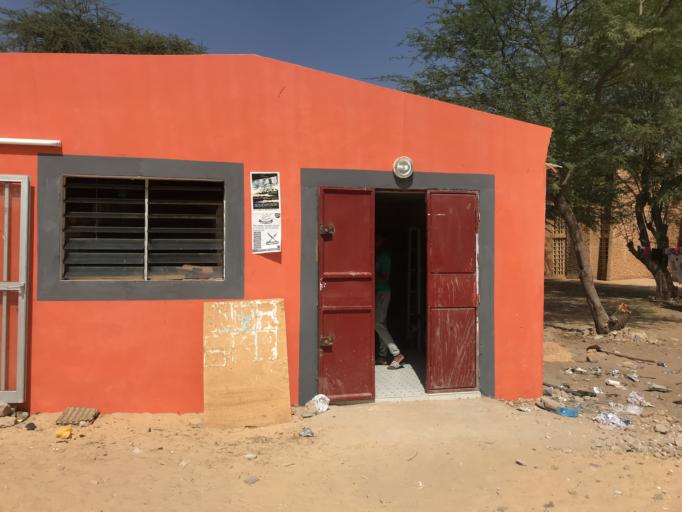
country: SN
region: Saint-Louis
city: Saint-Louis
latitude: 16.0660
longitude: -16.4224
